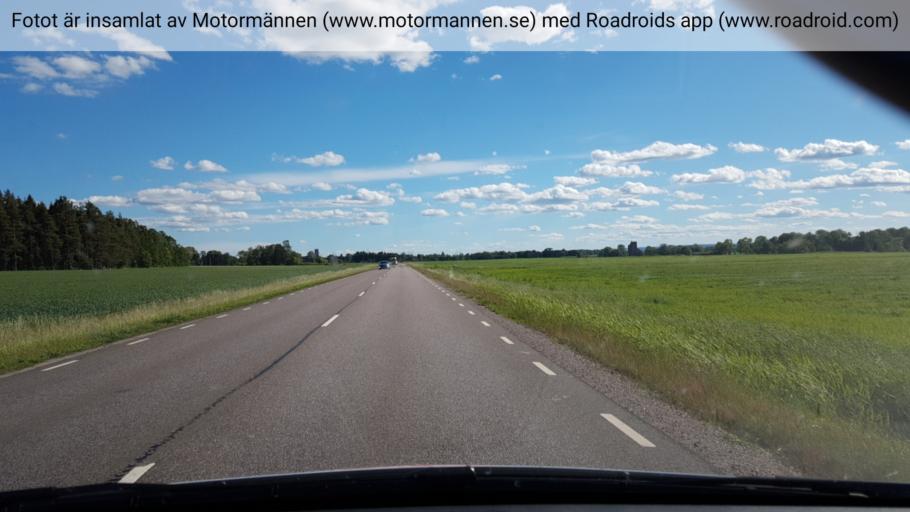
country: SE
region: Vaestra Goetaland
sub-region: Toreboda Kommun
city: Toereboda
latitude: 58.5948
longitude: 14.0092
